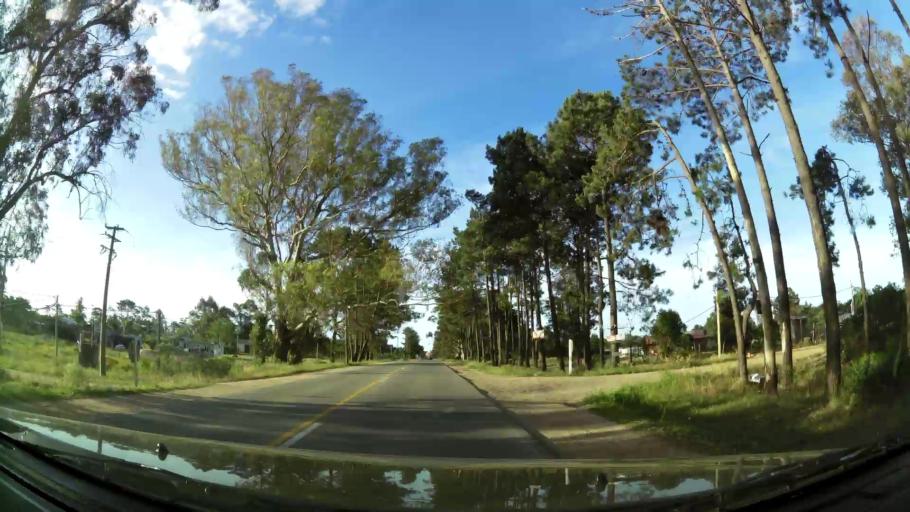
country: UY
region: Canelones
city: Atlantida
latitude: -34.7658
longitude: -55.8427
